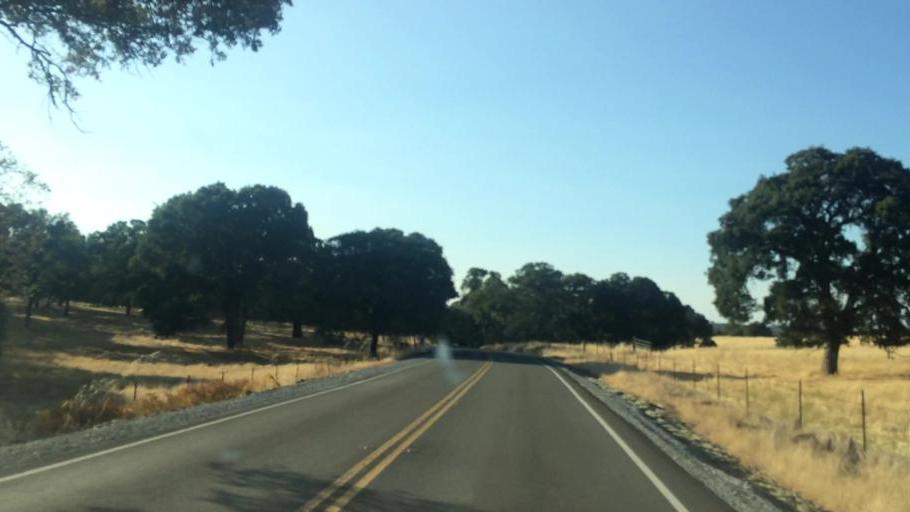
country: US
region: California
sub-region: Amador County
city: Plymouth
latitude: 38.5028
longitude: -120.9429
